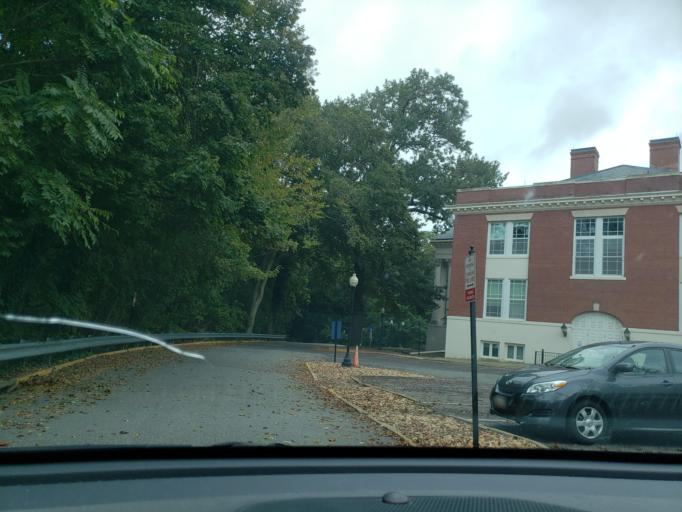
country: US
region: Virginia
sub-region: City of Fredericksburg
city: Fredericksburg
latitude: 38.3042
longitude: -77.4747
